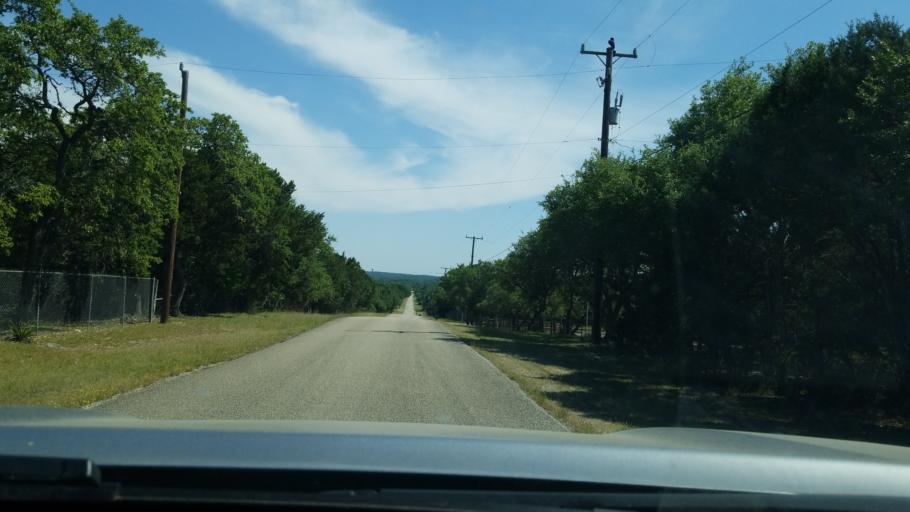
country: US
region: Texas
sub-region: Comal County
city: Bulverde
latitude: 29.7604
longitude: -98.5179
